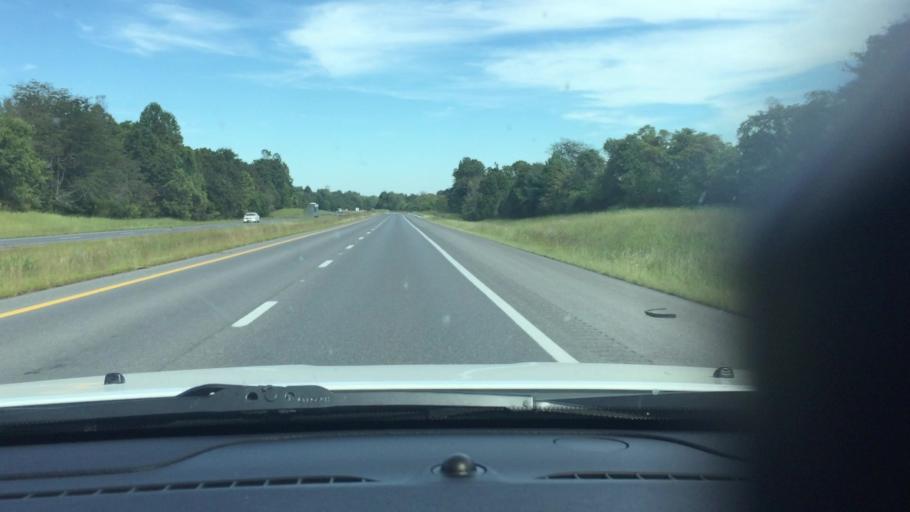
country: US
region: Kentucky
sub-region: Caldwell County
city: Princeton
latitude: 37.1141
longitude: -87.9313
